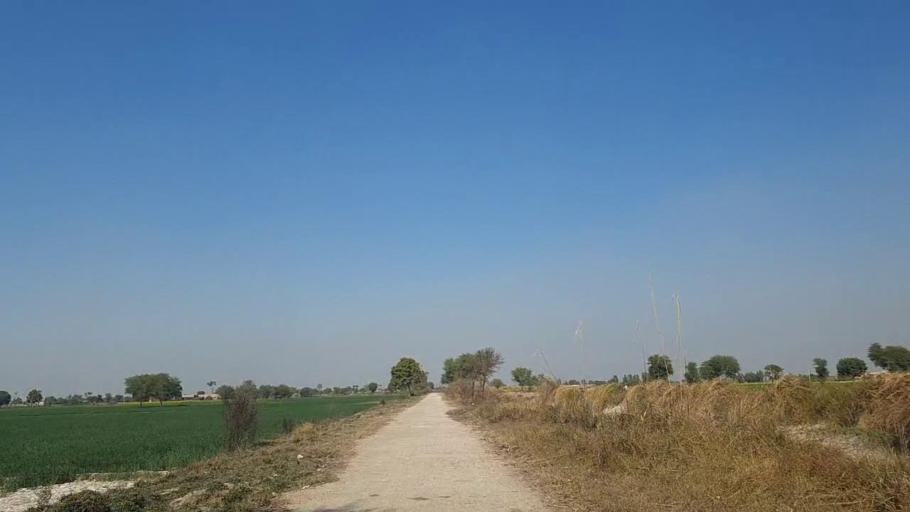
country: PK
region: Sindh
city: Sakrand
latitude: 26.2675
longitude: 68.2210
